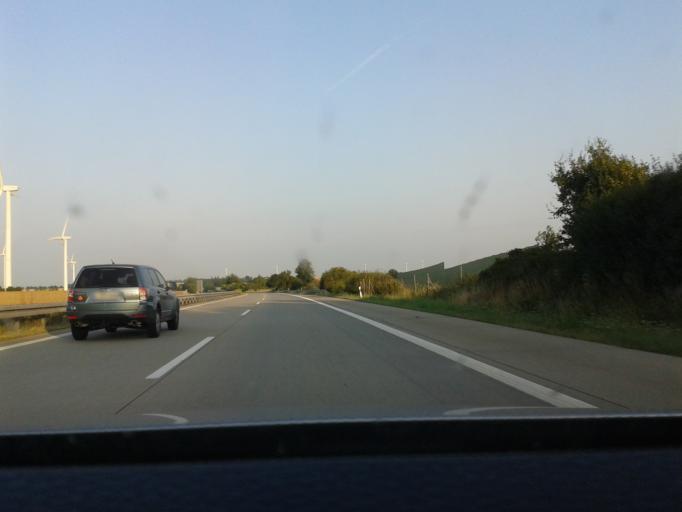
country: DE
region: Saxony
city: Bockelwitz
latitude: 51.1986
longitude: 12.9705
